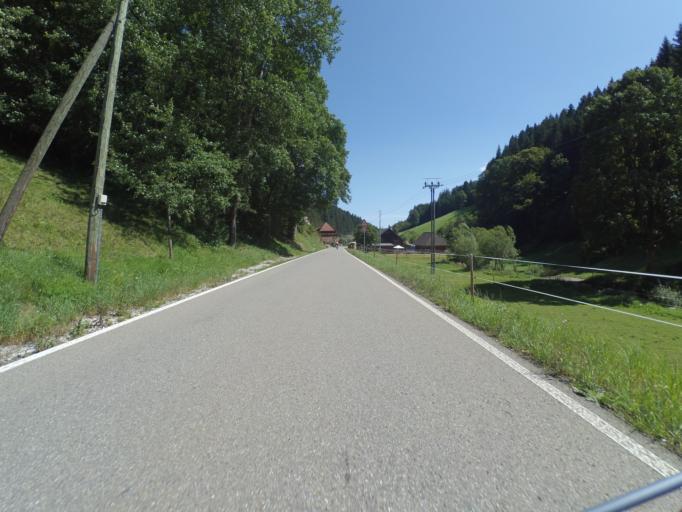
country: DE
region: Baden-Wuerttemberg
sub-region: Freiburg Region
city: Vohrenbach
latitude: 48.0225
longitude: 8.2724
